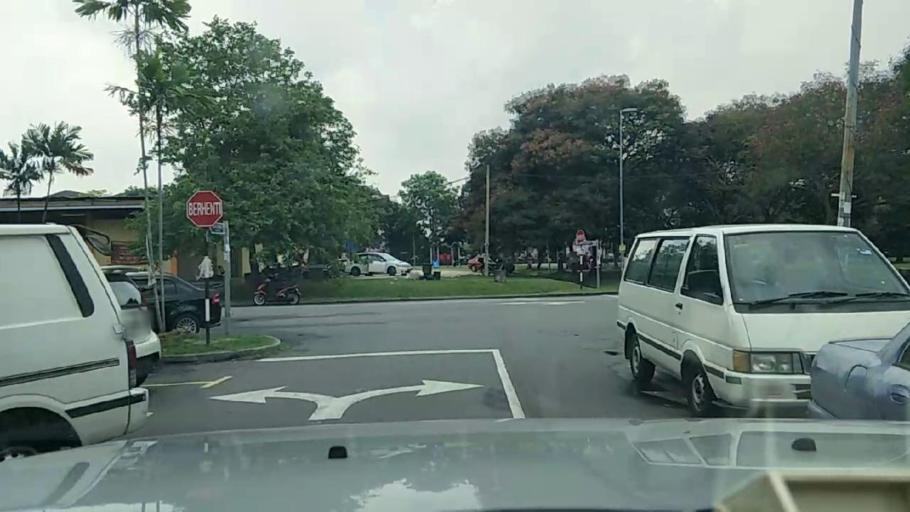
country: MY
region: Putrajaya
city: Putrajaya
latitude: 2.9466
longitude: 101.6190
